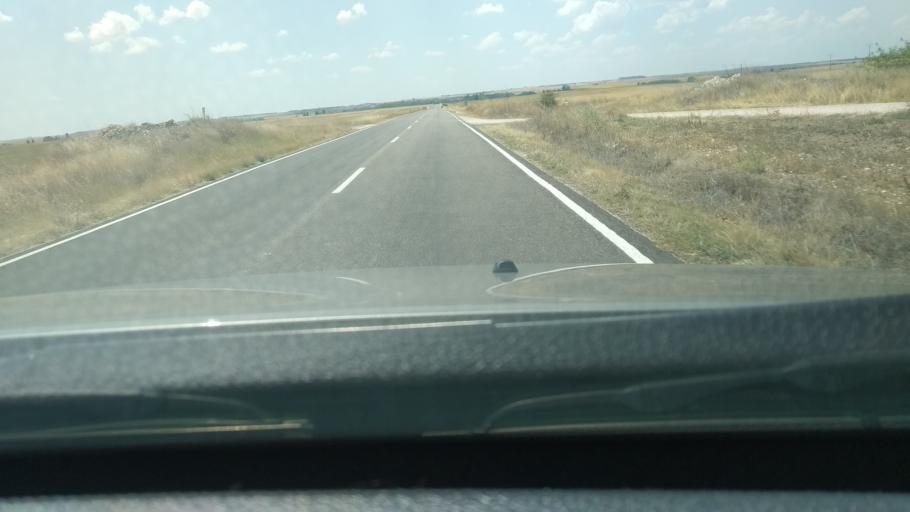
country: ES
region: Castille and Leon
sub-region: Provincia de Burgos
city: Villafruela
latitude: 41.9281
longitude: -3.8924
